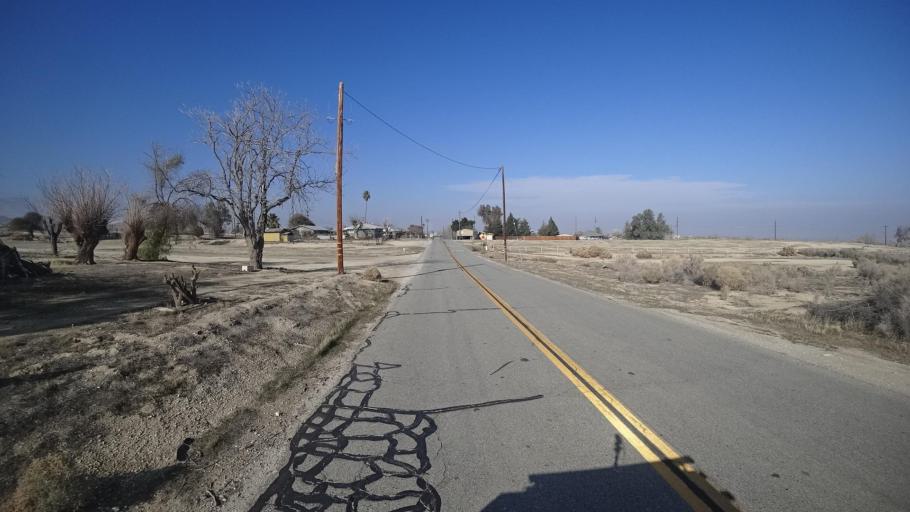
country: US
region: California
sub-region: Kern County
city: Taft Heights
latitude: 35.1748
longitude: -119.5384
